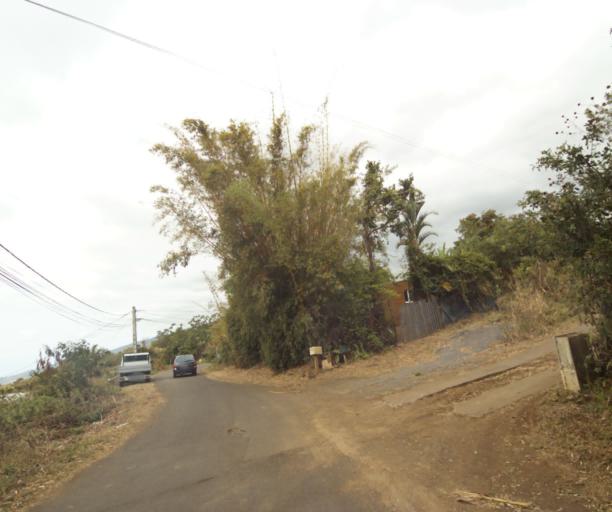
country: RE
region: Reunion
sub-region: Reunion
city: Saint-Paul
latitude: -21.0294
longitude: 55.2995
